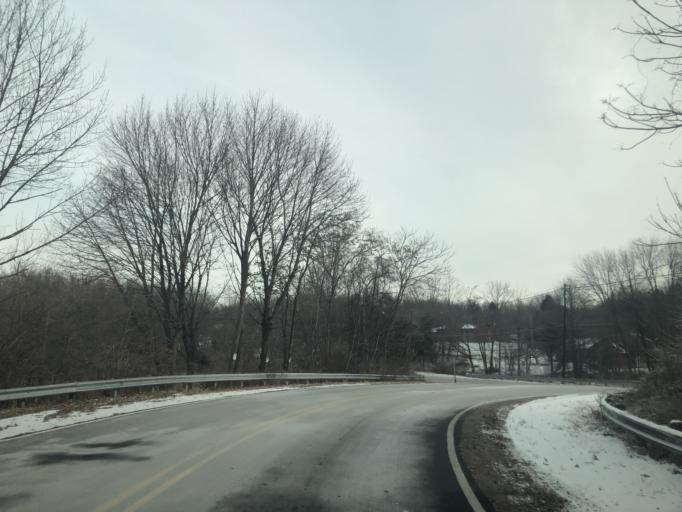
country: US
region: New Jersey
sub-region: Warren County
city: Belvidere
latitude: 40.9344
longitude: -75.0262
